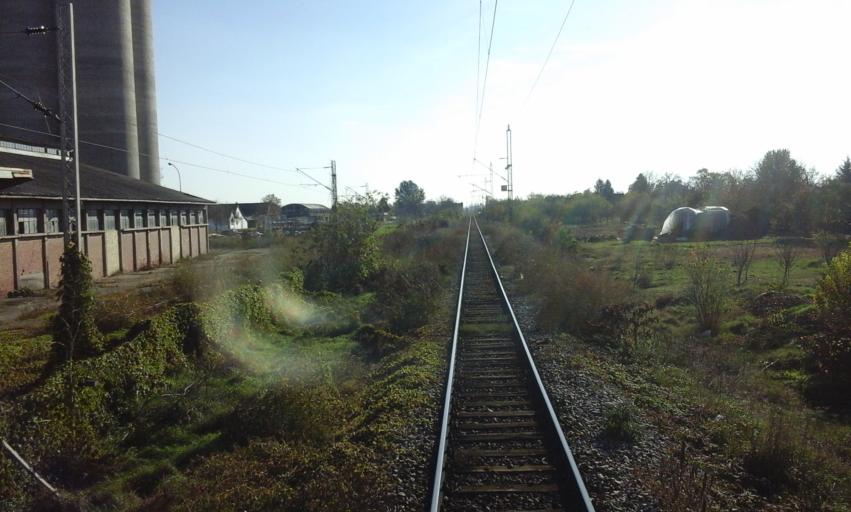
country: RS
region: Autonomna Pokrajina Vojvodina
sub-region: Severnobacki Okrug
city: Backa Topola
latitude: 45.8093
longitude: 19.6483
